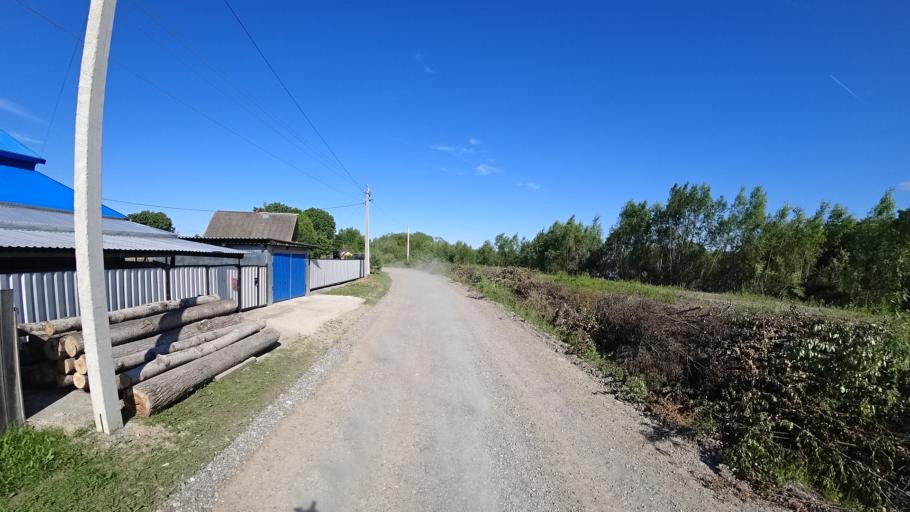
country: RU
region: Khabarovsk Krai
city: Khor
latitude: 47.8860
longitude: 135.0057
